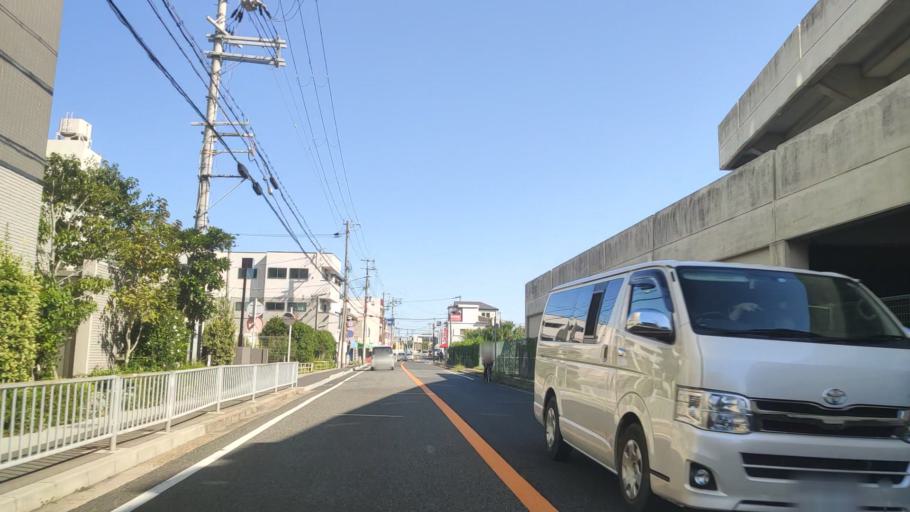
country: JP
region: Hyogo
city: Akashi
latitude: 34.6539
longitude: 134.9885
